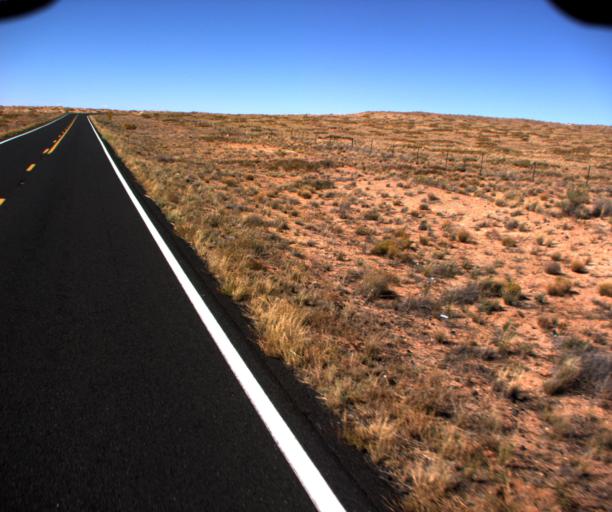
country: US
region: Arizona
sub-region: Coconino County
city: Tuba City
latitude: 36.0353
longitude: -111.1809
